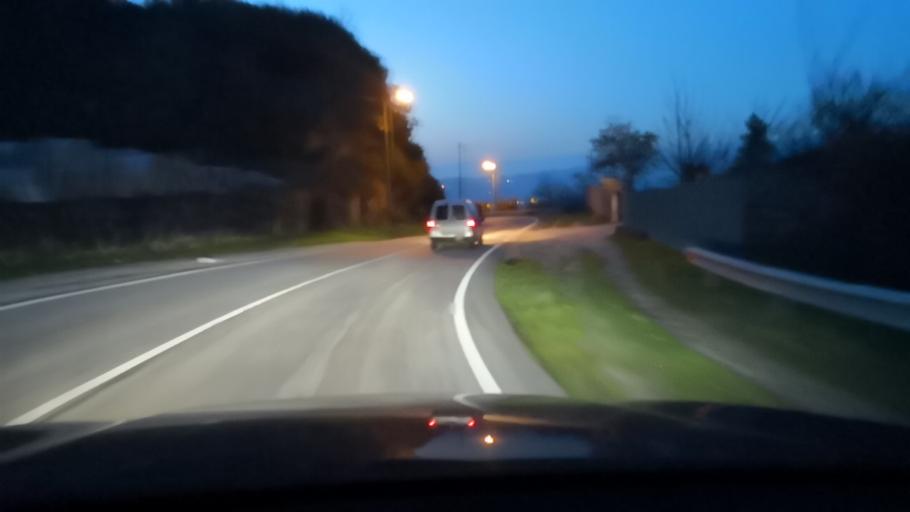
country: PT
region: Porto
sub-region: Baiao
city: Baiao
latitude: 41.2287
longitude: -8.0095
